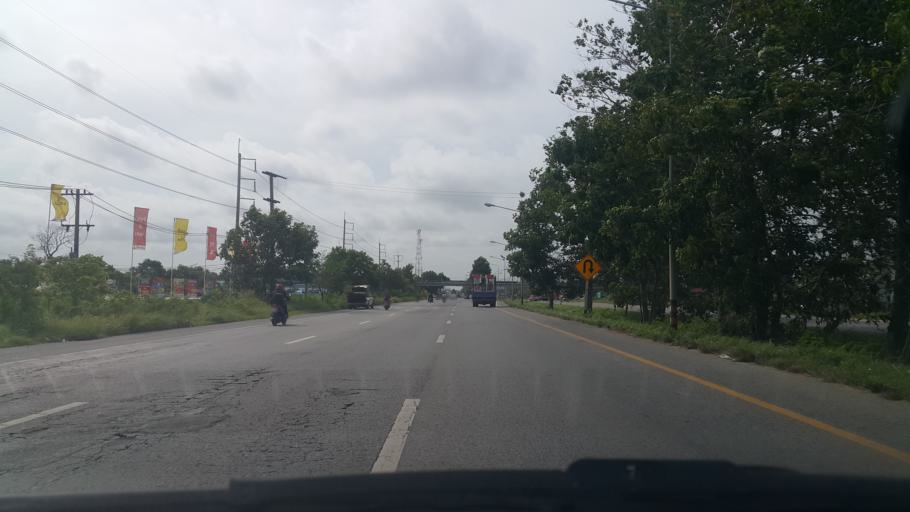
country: TH
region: Rayong
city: Rayong
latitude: 12.6717
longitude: 101.3052
